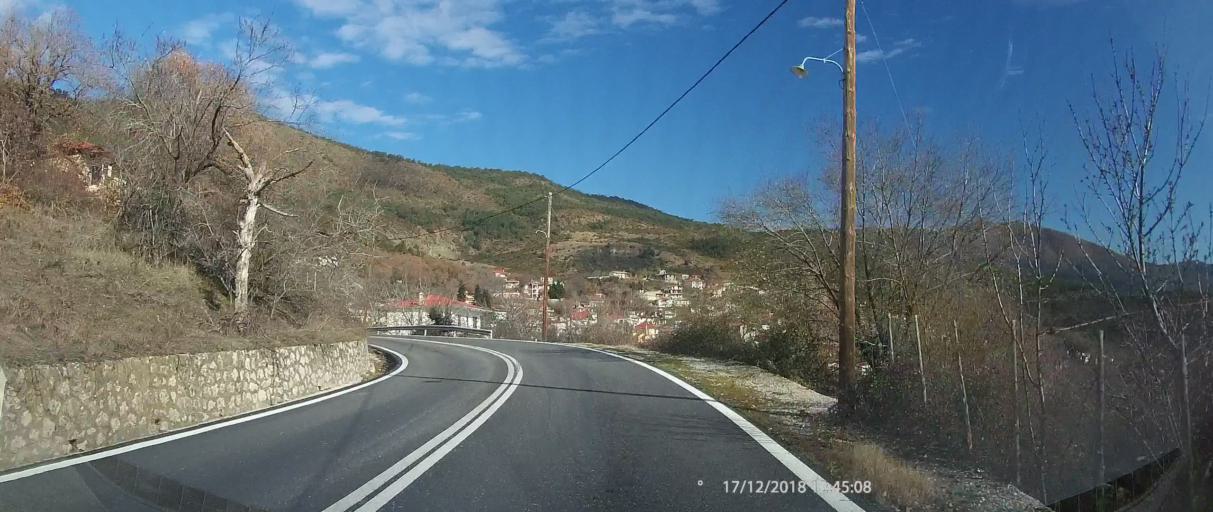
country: GR
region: Thessaly
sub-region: Trikala
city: Kastraki
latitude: 39.7865
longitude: 21.4075
